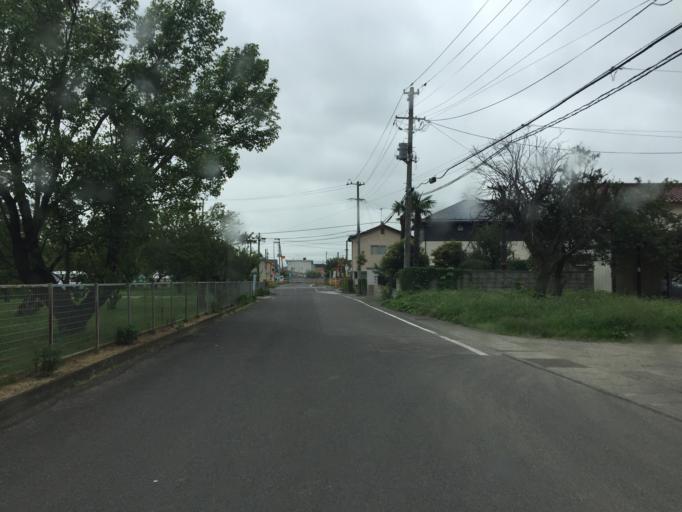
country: JP
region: Fukushima
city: Fukushima-shi
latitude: 37.7735
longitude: 140.3840
